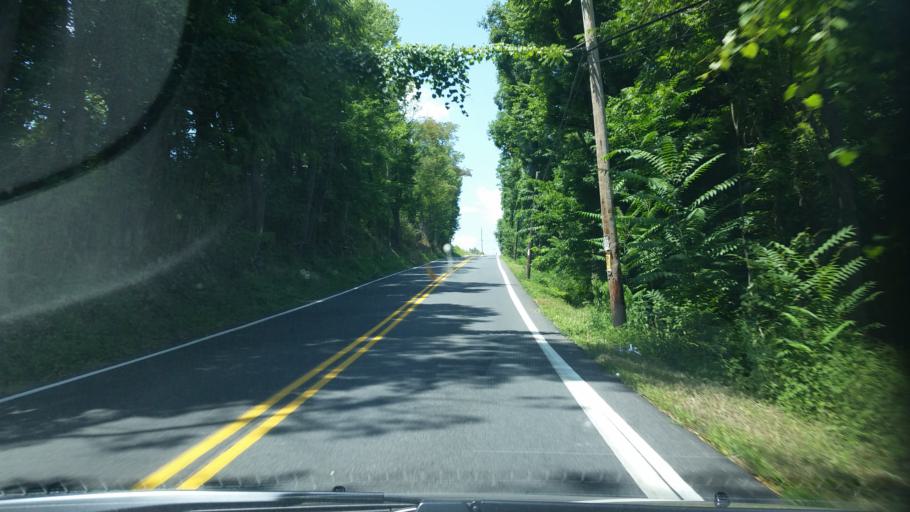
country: US
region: Pennsylvania
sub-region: Dauphin County
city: Rutherford
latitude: 40.2869
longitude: -76.7433
